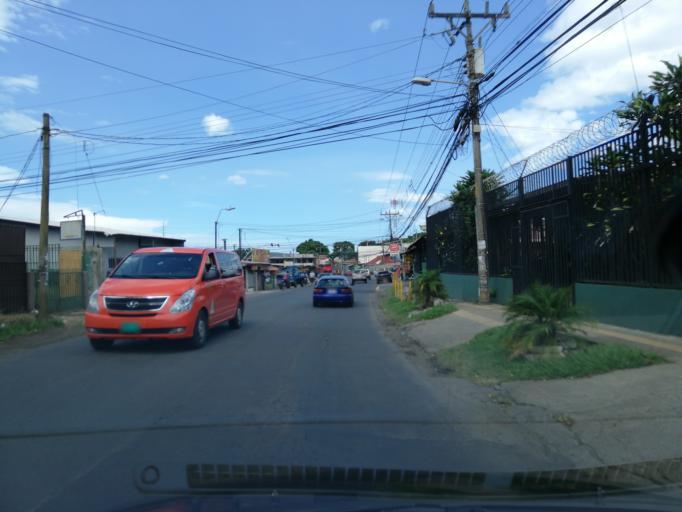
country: CR
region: Alajuela
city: Alajuela
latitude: 9.9919
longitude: -84.2358
